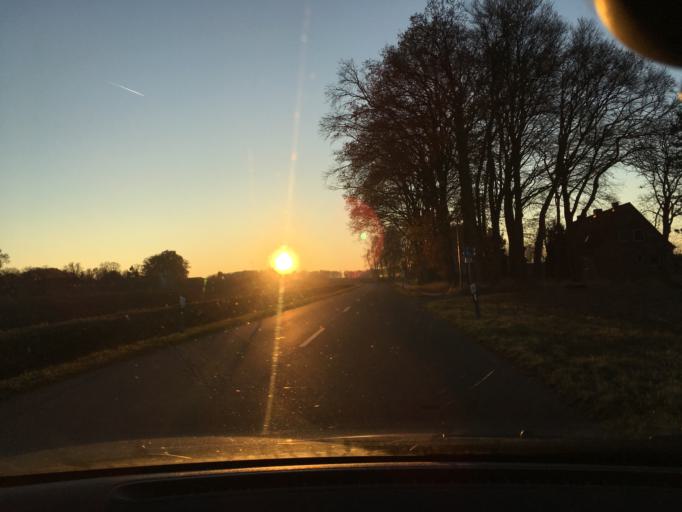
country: DE
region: Lower Saxony
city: Natendorf
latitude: 53.0609
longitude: 10.4563
